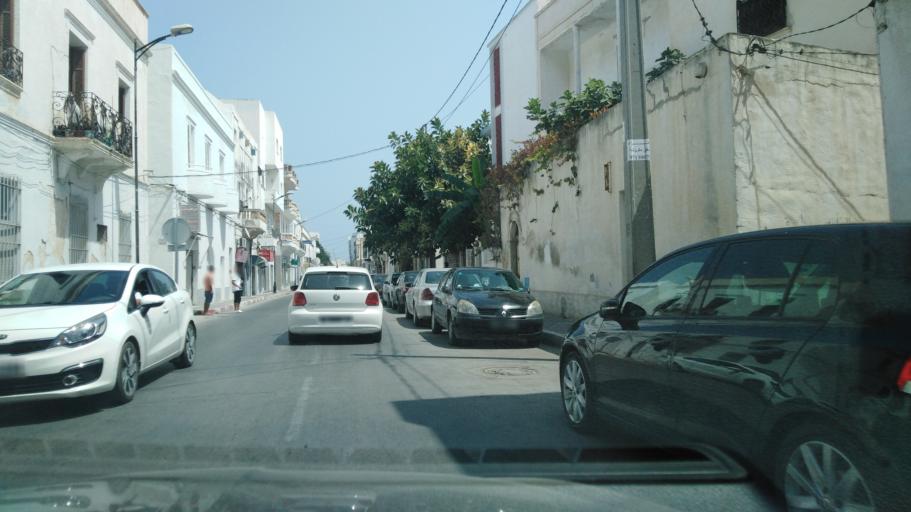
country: TN
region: Al Mahdiyah
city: Mahdia
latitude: 35.5066
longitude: 11.0590
